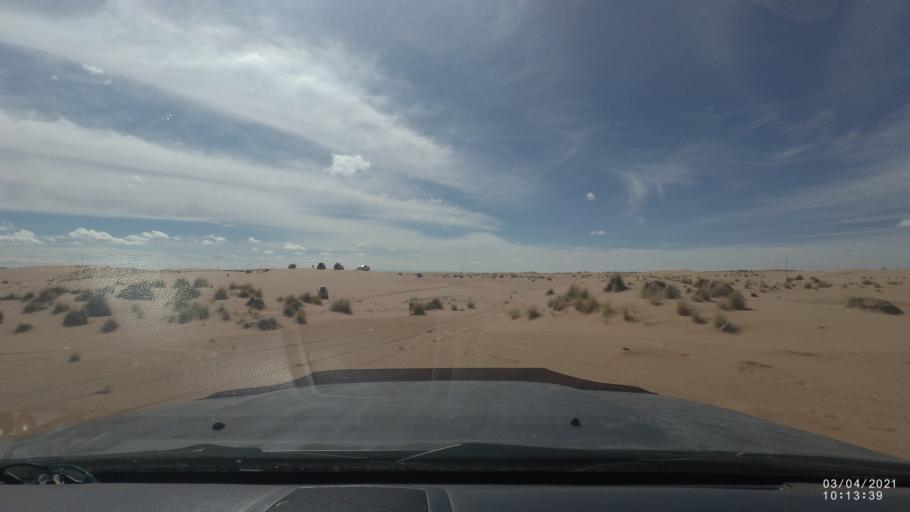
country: BO
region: Oruro
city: Poopo
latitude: -18.7045
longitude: -67.5274
